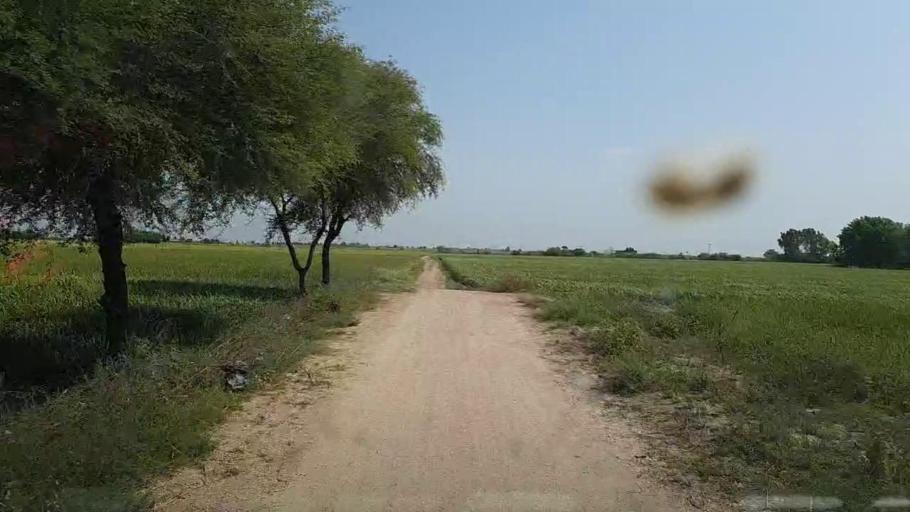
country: PK
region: Sindh
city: Kario
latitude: 24.6331
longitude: 68.5438
